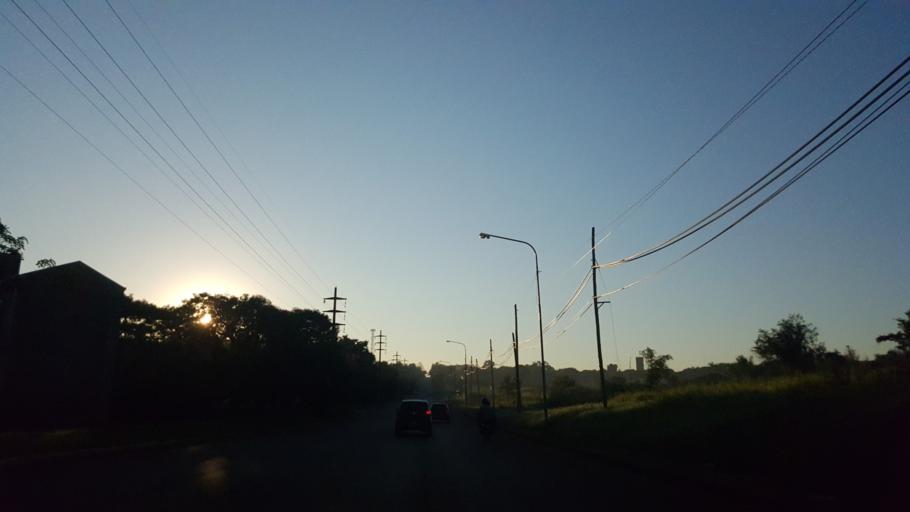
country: AR
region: Misiones
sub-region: Departamento de Capital
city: Posadas
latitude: -27.3735
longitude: -55.9361
